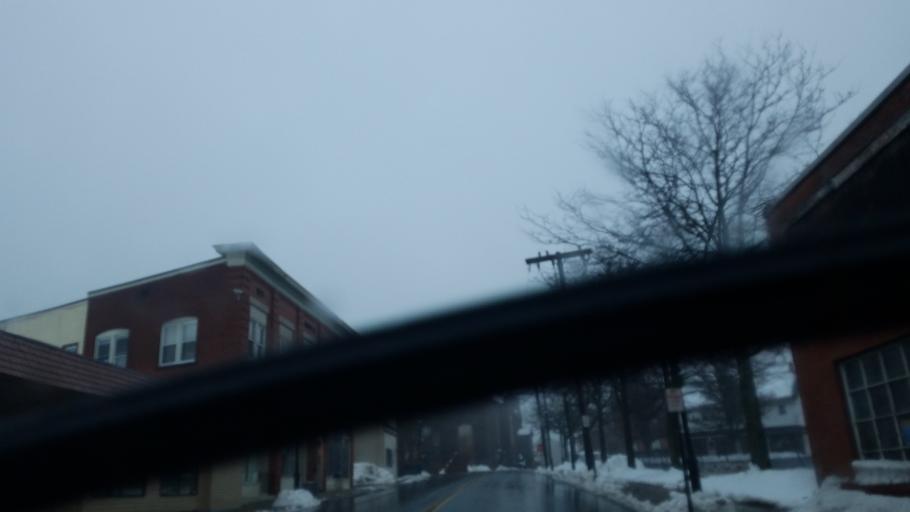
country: US
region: Connecticut
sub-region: Hartford County
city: Thompsonville
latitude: 41.9978
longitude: -72.5999
